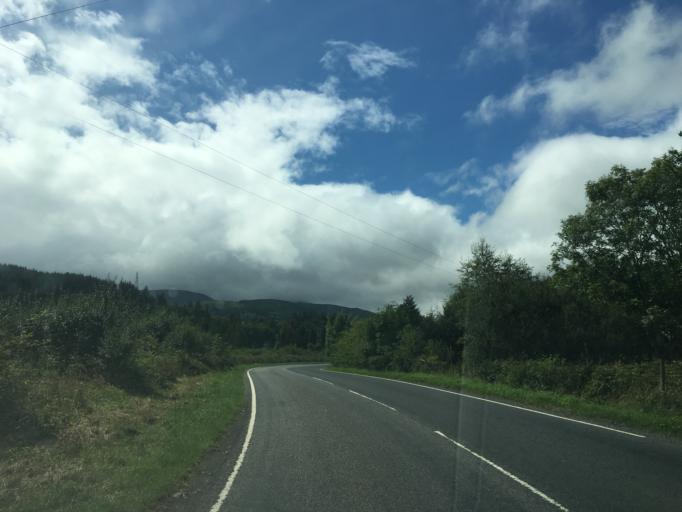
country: GB
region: Scotland
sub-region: Argyll and Bute
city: Dunoon
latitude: 55.9958
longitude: -4.9741
